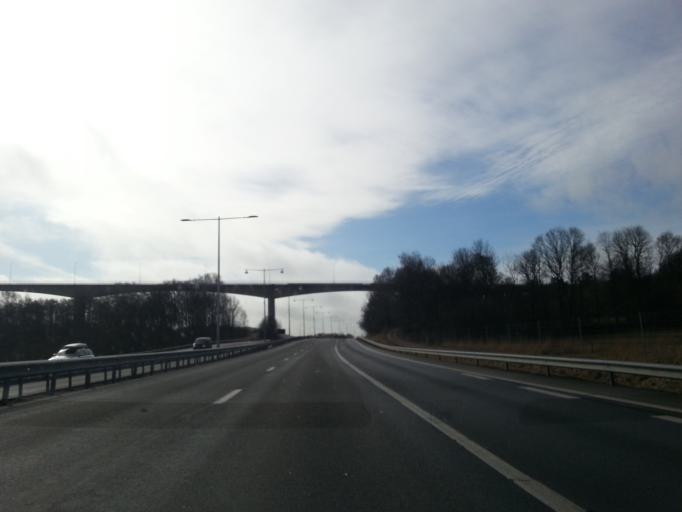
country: SE
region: Vaestra Goetaland
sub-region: Goteborg
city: Gardsten
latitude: 57.8033
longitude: 12.0076
